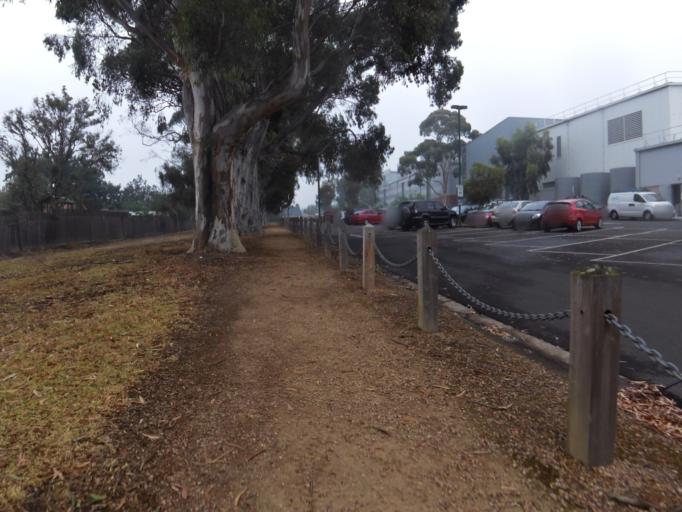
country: AU
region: Victoria
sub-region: Whitehorse
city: Box Hill South
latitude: -37.8258
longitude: 145.1184
